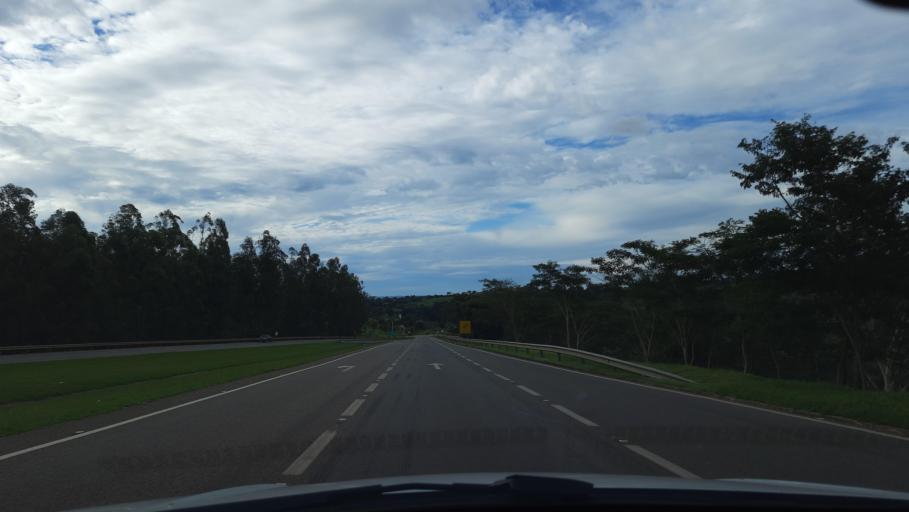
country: BR
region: Sao Paulo
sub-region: Sao Joao Da Boa Vista
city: Sao Joao da Boa Vista
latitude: -21.9638
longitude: -46.8332
